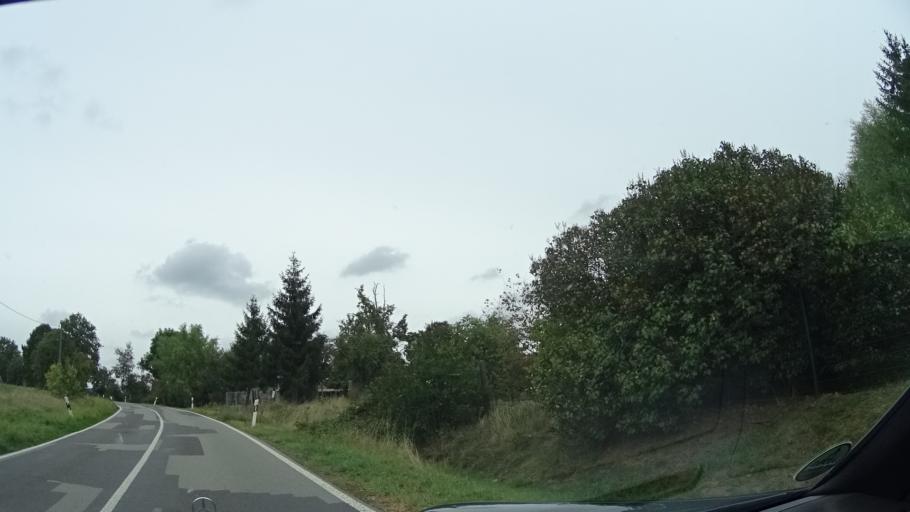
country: DE
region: Brandenburg
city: Walsleben
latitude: 52.9556
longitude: 12.7074
